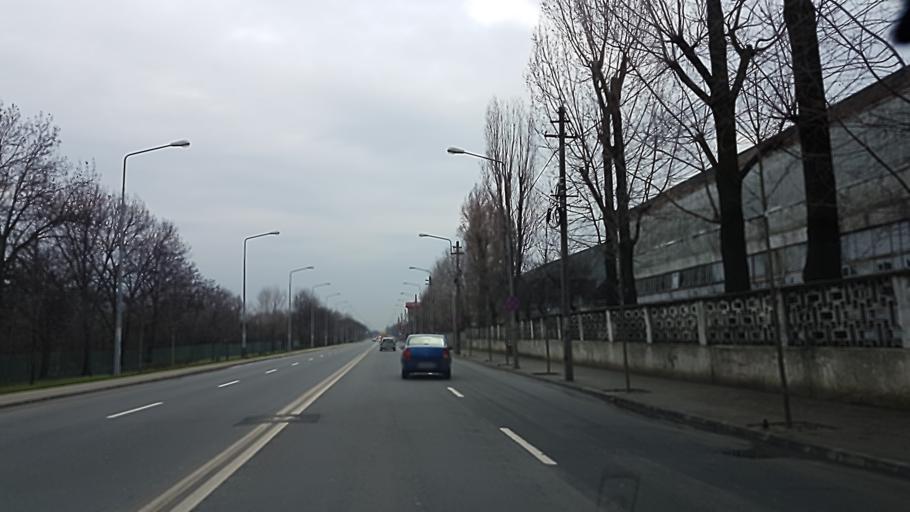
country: RO
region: Ilfov
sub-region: Comuna Pantelimon
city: Pantelimon
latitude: 44.4393
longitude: 26.1944
